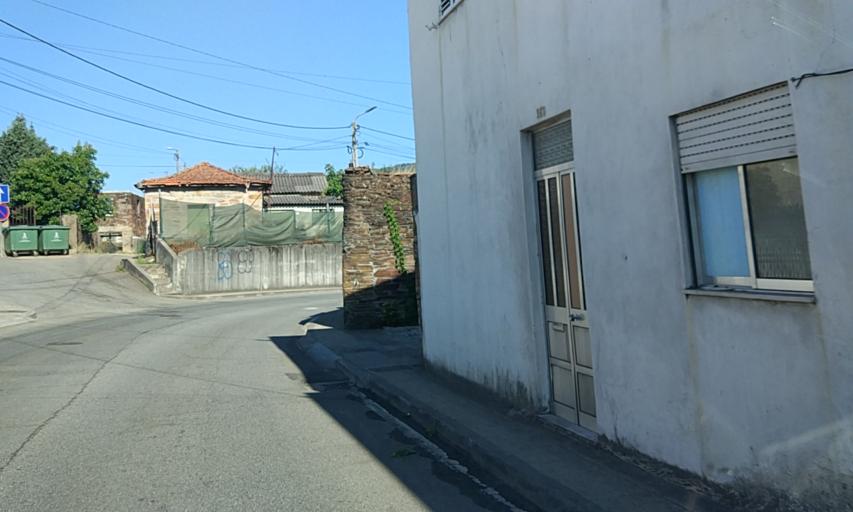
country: PT
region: Porto
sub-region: Santo Tirso
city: Santo Tirso
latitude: 41.3390
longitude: -8.4850
